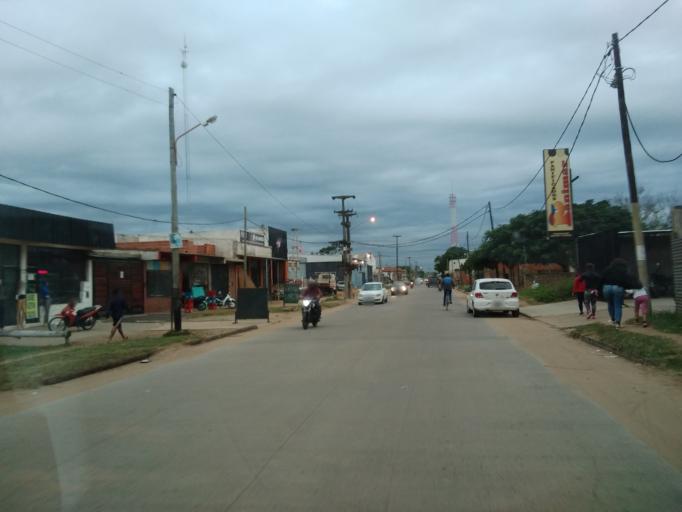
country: AR
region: Corrientes
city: Corrientes
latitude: -27.5048
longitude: -58.7952
